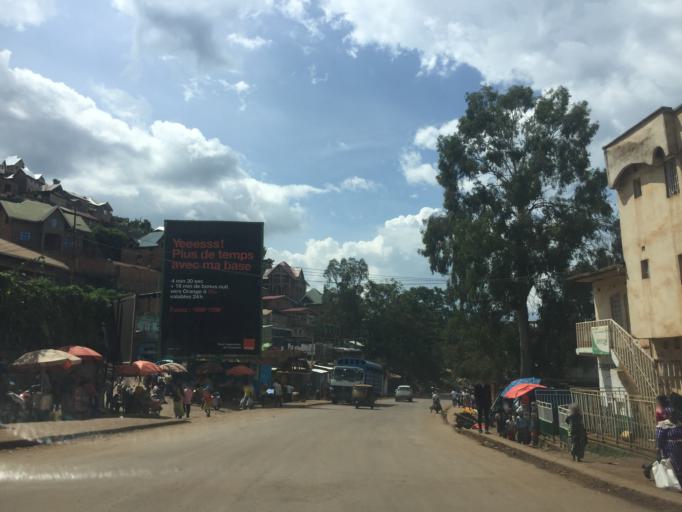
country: CD
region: South Kivu
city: Bukavu
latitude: -2.4937
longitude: 28.8495
